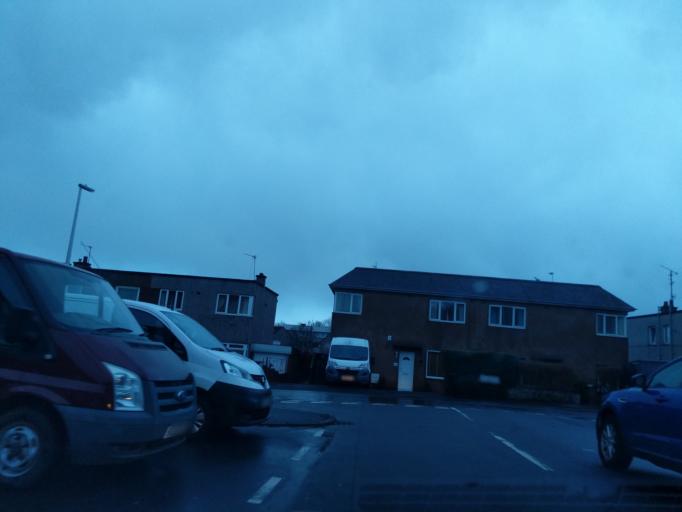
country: GB
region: Scotland
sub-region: West Lothian
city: Seafield
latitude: 55.9501
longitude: -3.1339
